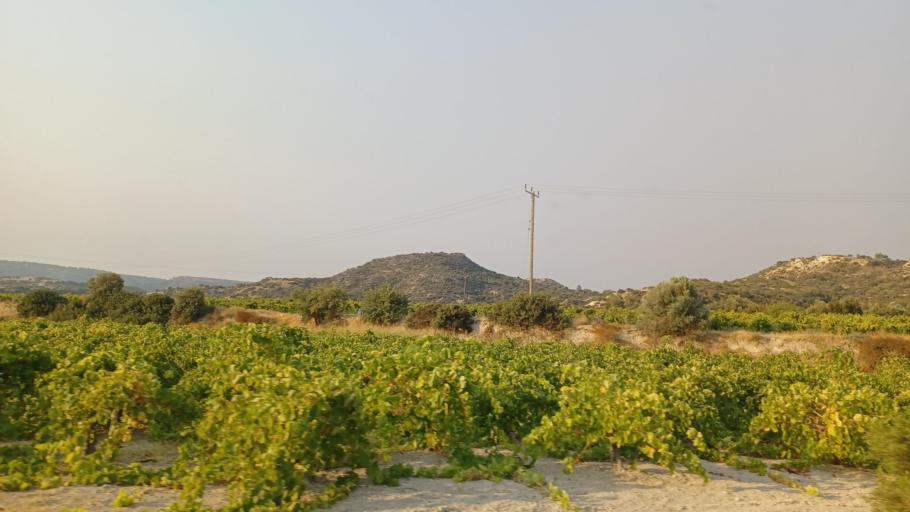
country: CY
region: Limassol
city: Pissouri
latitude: 34.7008
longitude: 32.6663
